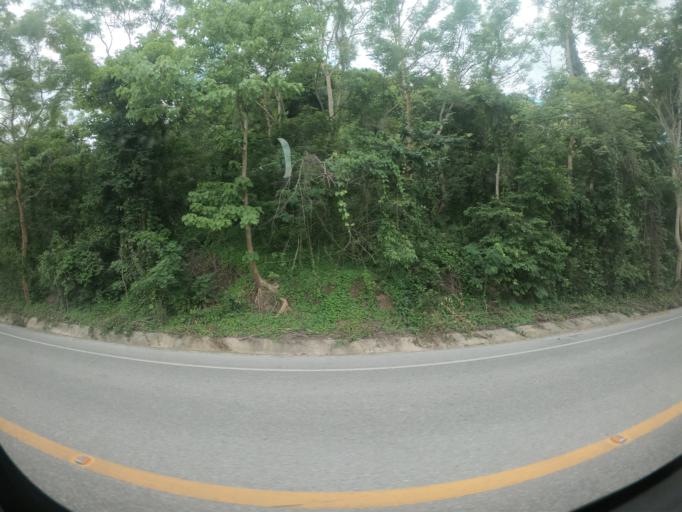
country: TH
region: Nakhon Nayok
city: Nakhon Nayok
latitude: 14.3155
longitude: 101.3166
